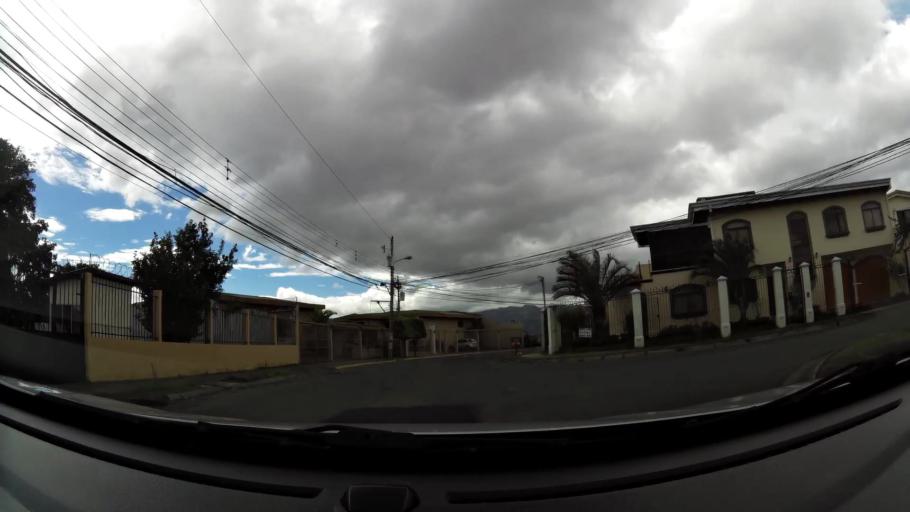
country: CR
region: San Jose
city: Curridabat
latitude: 9.9217
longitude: -84.0405
